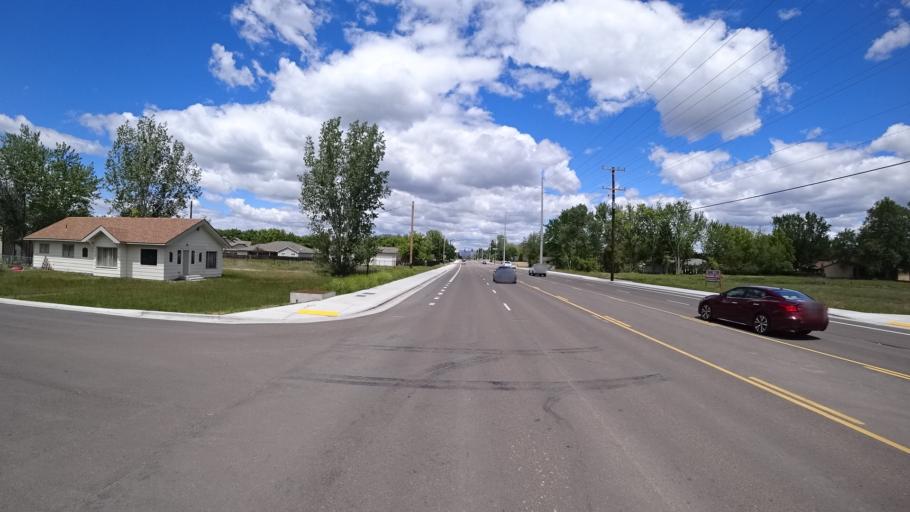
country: US
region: Idaho
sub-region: Ada County
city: Eagle
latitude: 43.6405
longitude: -116.3344
